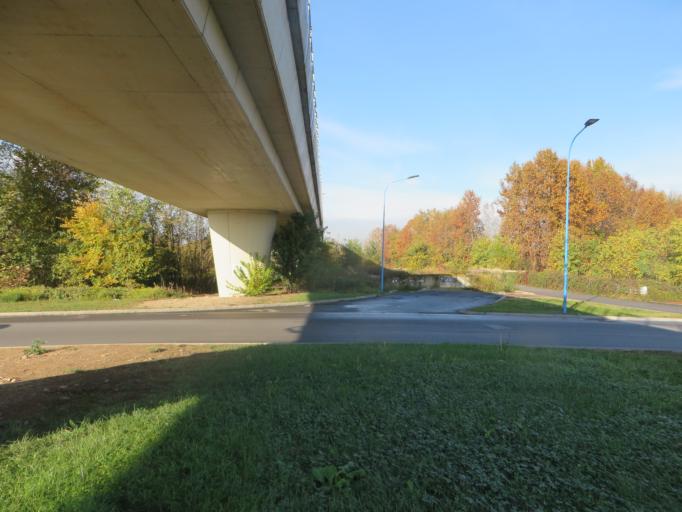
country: IT
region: Lombardy
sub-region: Provincia di Brescia
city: Buffalora-Bettole
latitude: 45.5117
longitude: 10.2788
